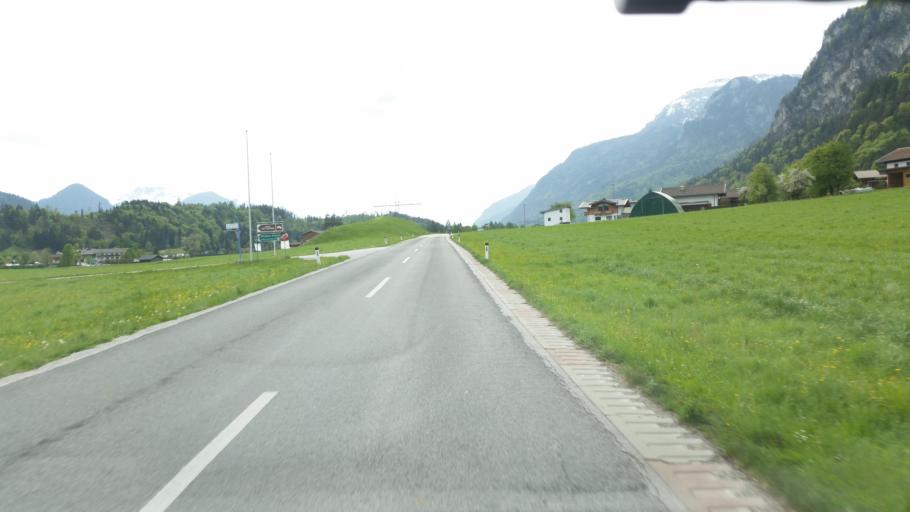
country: AT
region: Tyrol
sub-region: Politischer Bezirk Kufstein
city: Radfeld
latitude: 47.4667
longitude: 11.9107
